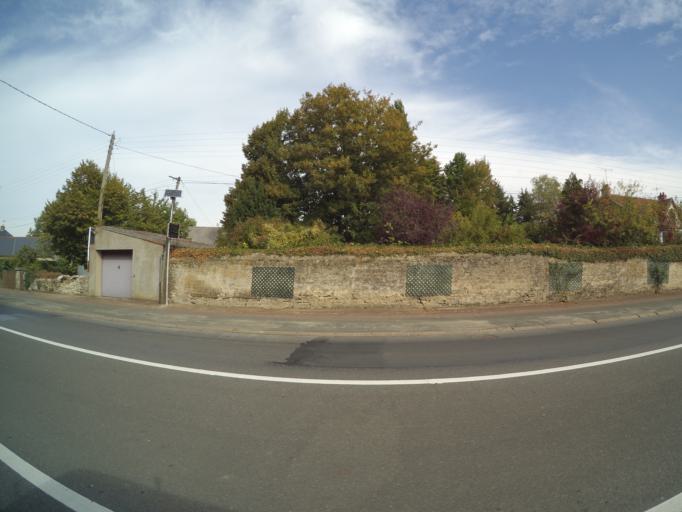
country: FR
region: Pays de la Loire
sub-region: Departement de Maine-et-Loire
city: Doue-la-Fontaine
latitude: 47.1987
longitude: -0.2775
